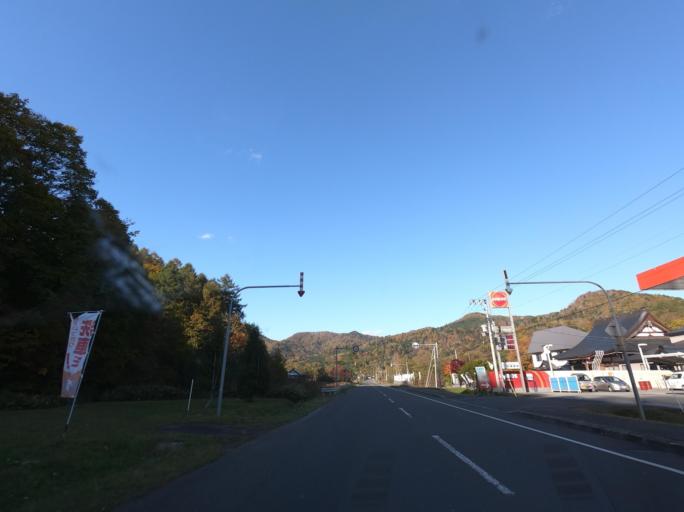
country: JP
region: Hokkaido
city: Iwamizawa
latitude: 43.0009
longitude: 142.0045
